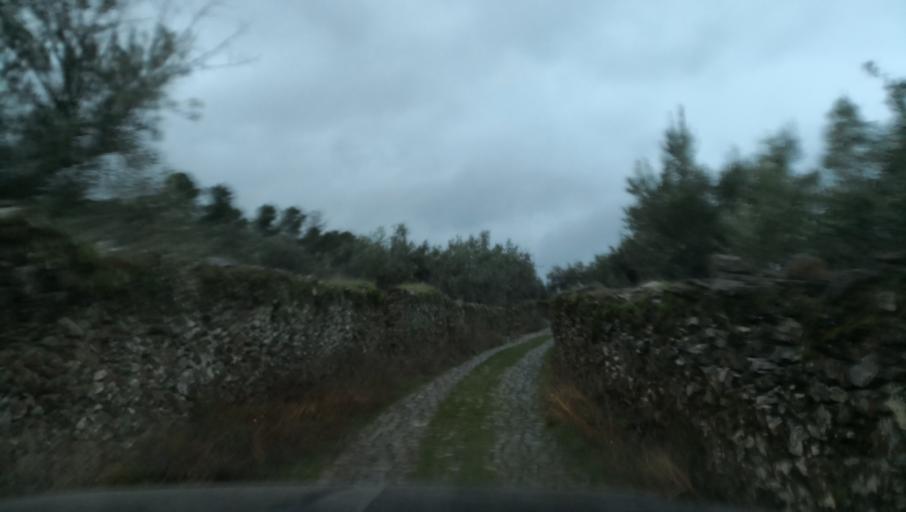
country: PT
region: Vila Real
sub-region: Vila Real
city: Vila Real
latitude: 41.2506
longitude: -7.7381
